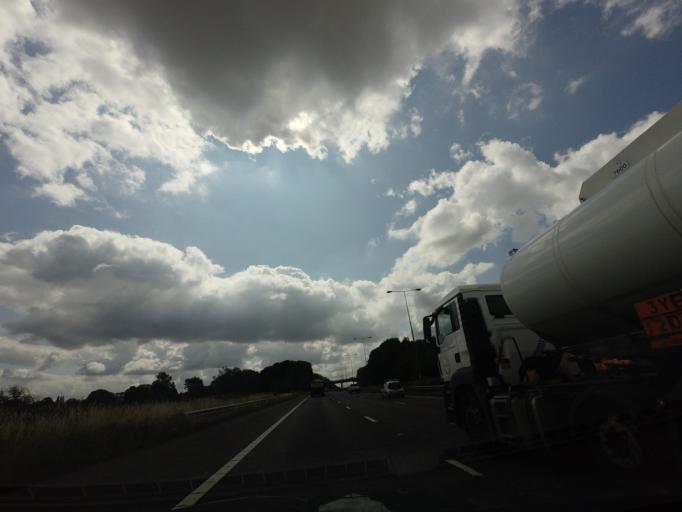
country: GB
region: England
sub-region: Borough of Wigan
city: Shevington
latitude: 53.5411
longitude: -2.6970
